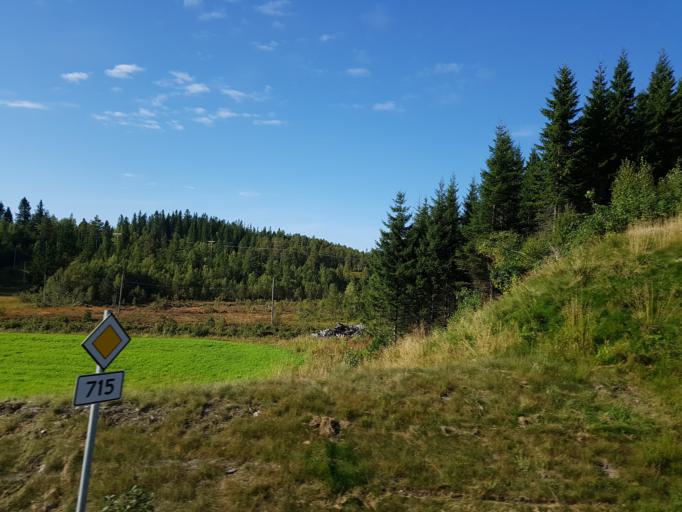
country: NO
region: Sor-Trondelag
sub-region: Trondheim
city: Trondheim
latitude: 63.6497
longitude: 10.2652
